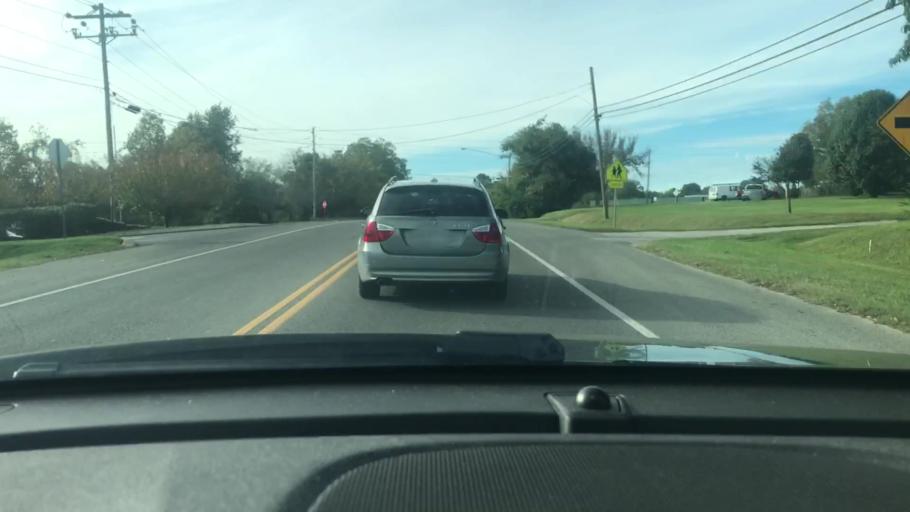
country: US
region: Tennessee
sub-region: Williamson County
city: Franklin
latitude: 35.9254
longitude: -86.8831
